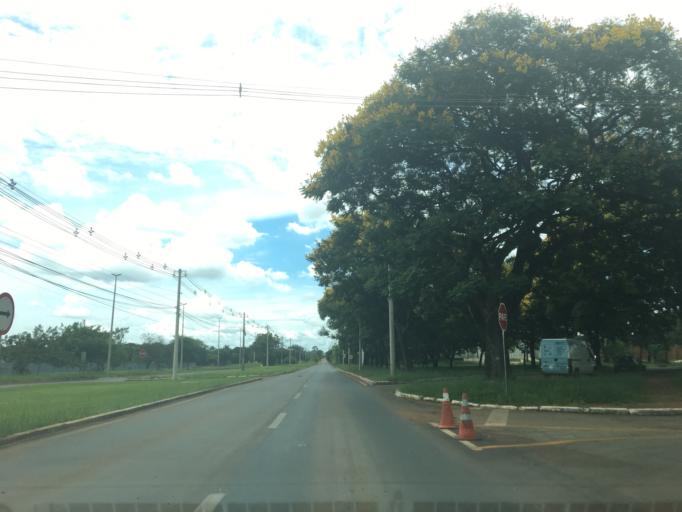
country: BR
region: Federal District
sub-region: Brasilia
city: Brasilia
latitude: -15.8277
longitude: -47.9349
